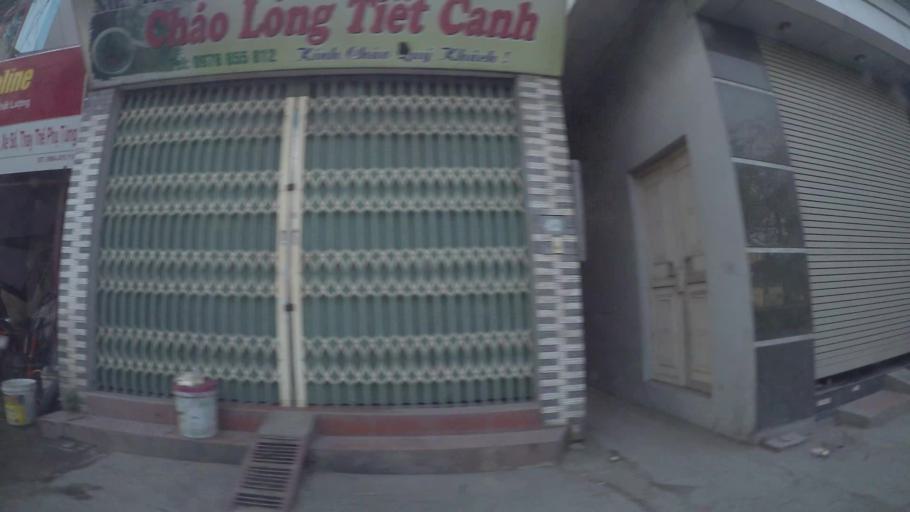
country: VN
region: Ha Noi
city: Van Dien
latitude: 20.9425
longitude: 105.8416
